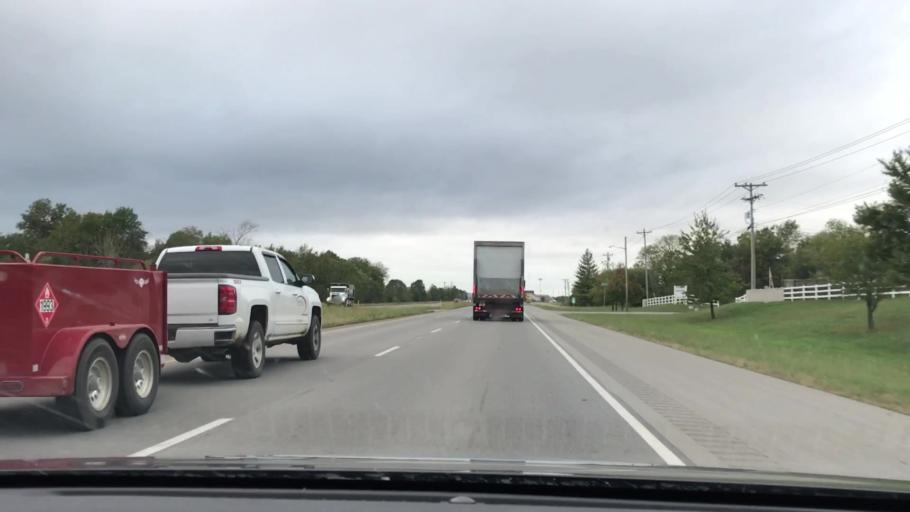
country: US
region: Kentucky
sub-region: Christian County
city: Hopkinsville
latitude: 36.8182
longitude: -87.4913
